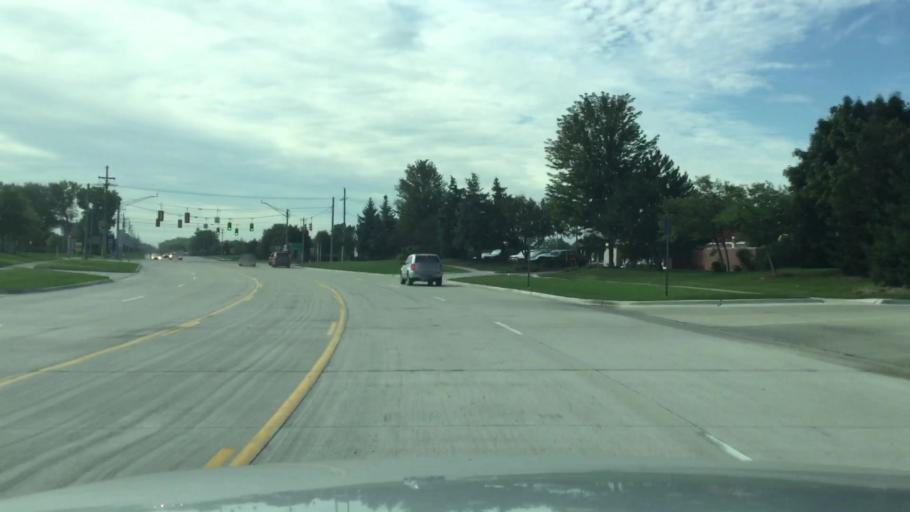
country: US
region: Michigan
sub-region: Wayne County
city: Canton
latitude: 42.2733
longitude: -83.4874
